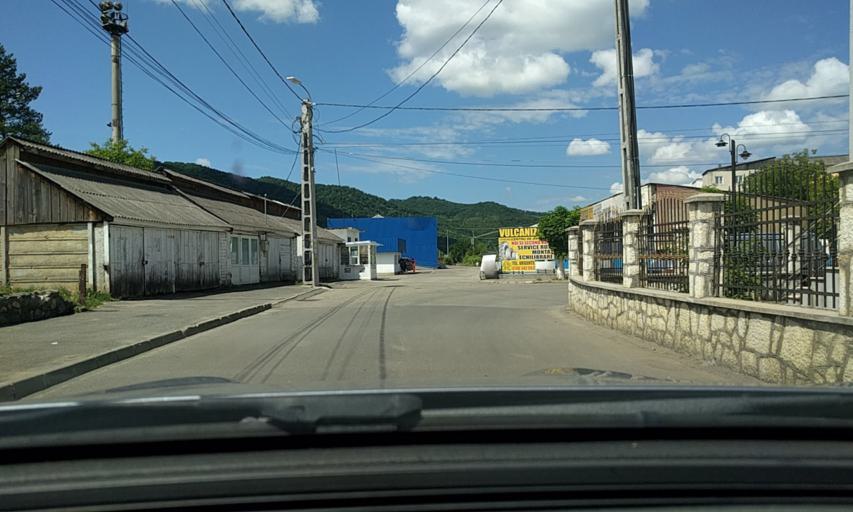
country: RO
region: Bistrita-Nasaud
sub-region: Oras Nasaud
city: Nasaud
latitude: 47.2815
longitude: 24.4096
